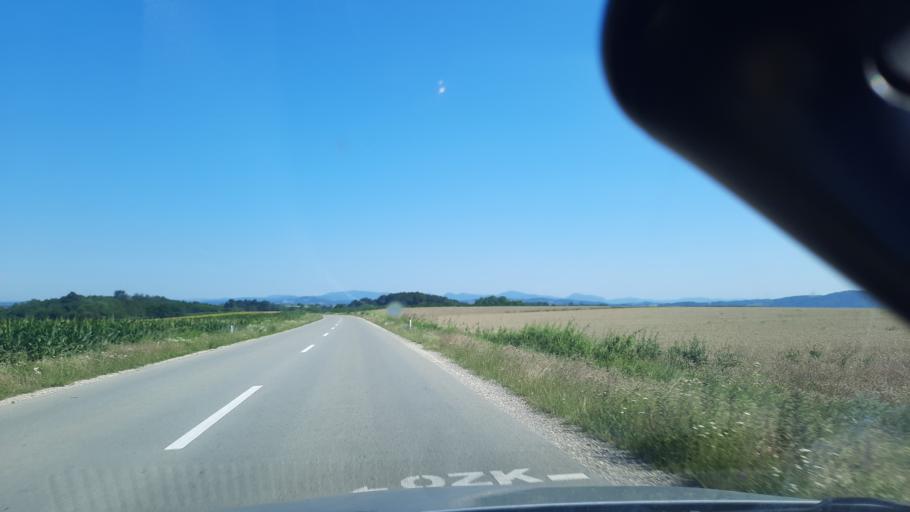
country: RS
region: Central Serbia
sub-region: Branicevski Okrug
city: Malo Crnice
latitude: 44.5620
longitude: 21.4352
